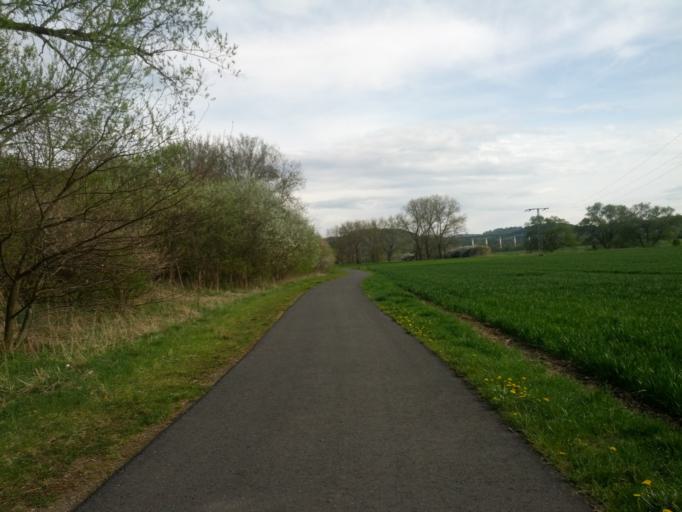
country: DE
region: Thuringia
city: Creuzburg
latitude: 51.0354
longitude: 10.2278
